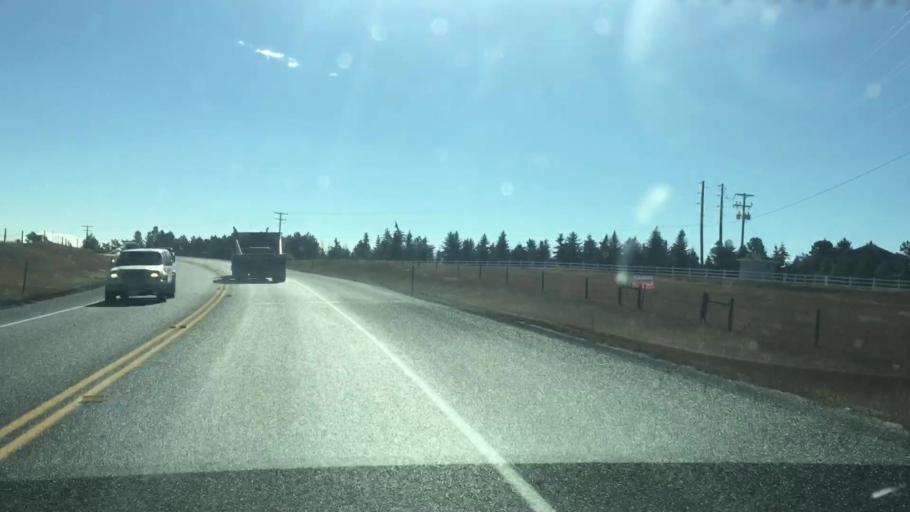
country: US
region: Colorado
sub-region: Elbert County
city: Ponderosa Park
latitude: 39.3627
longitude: -104.6709
